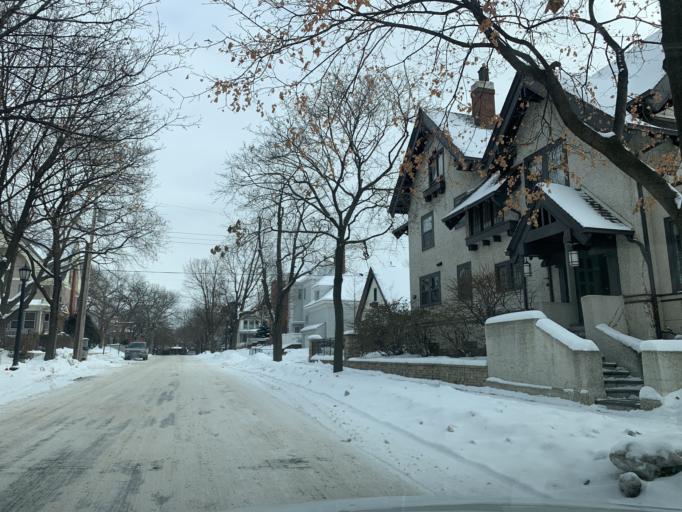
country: US
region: Minnesota
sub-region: Hennepin County
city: Minneapolis
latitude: 44.9645
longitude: -93.3007
